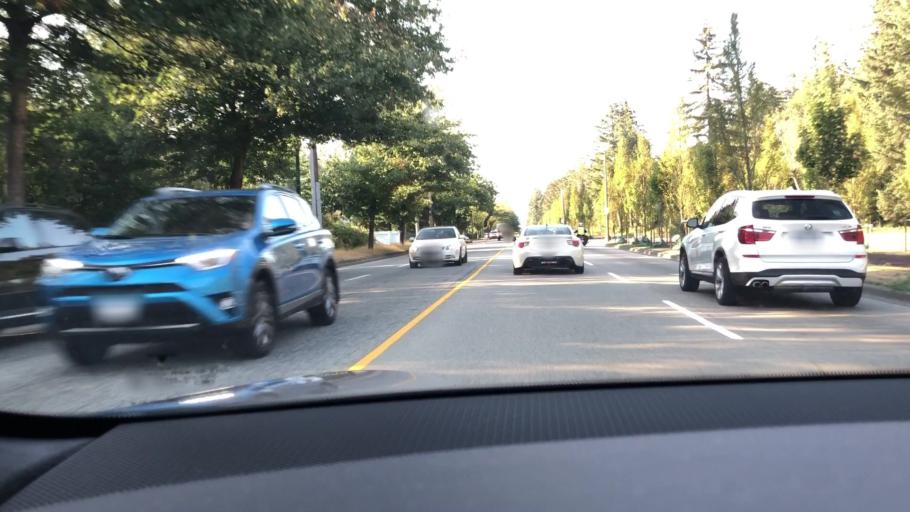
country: CA
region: British Columbia
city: Burnaby
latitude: 49.2240
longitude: -123.0235
